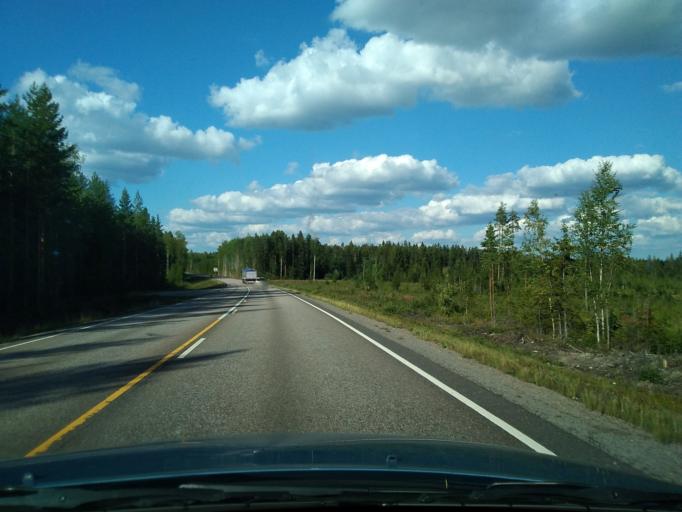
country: FI
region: Pirkanmaa
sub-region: Ylae-Pirkanmaa
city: Maenttae
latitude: 62.1039
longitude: 24.7370
